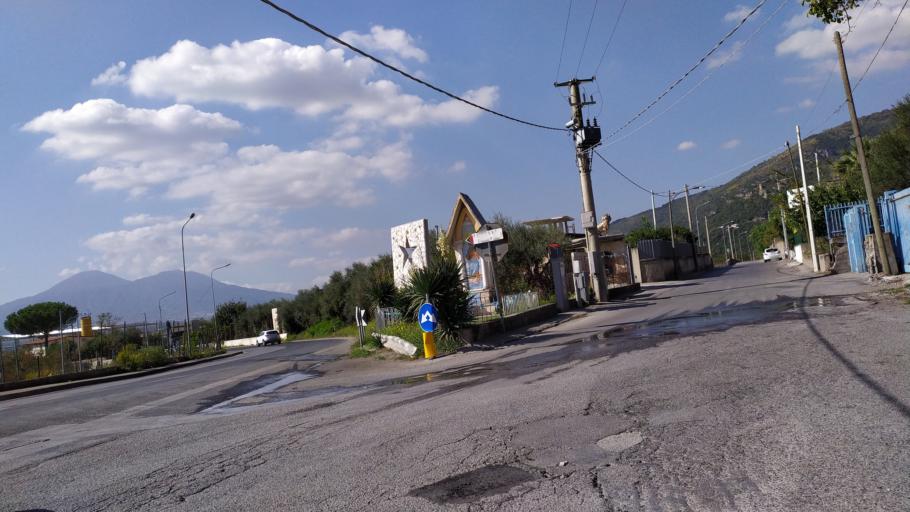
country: IT
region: Campania
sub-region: Provincia di Salerno
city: Sarno
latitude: 40.8251
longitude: 14.6029
